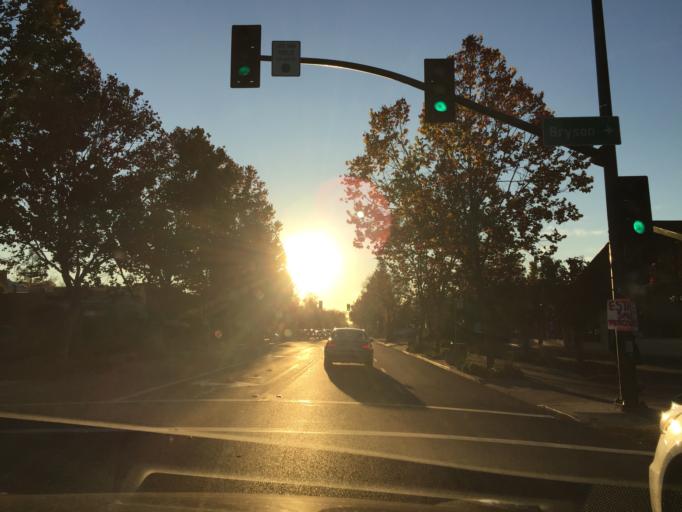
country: US
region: California
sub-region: Santa Clara County
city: Palo Alto
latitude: 37.4336
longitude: -122.1297
